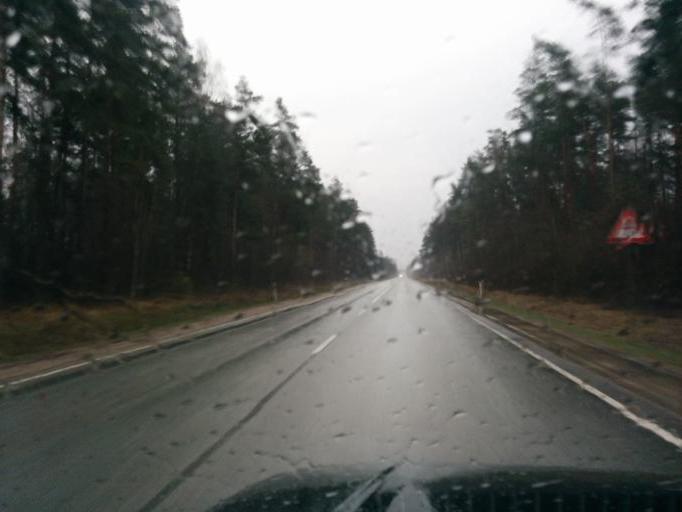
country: LV
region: Kekava
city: Kekava
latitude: 56.8107
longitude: 24.2221
